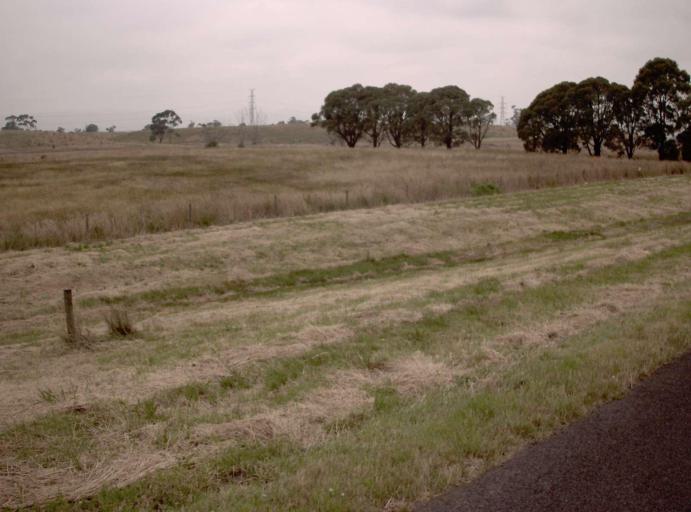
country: AU
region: Victoria
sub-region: Latrobe
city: Morwell
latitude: -38.2506
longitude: 146.3325
